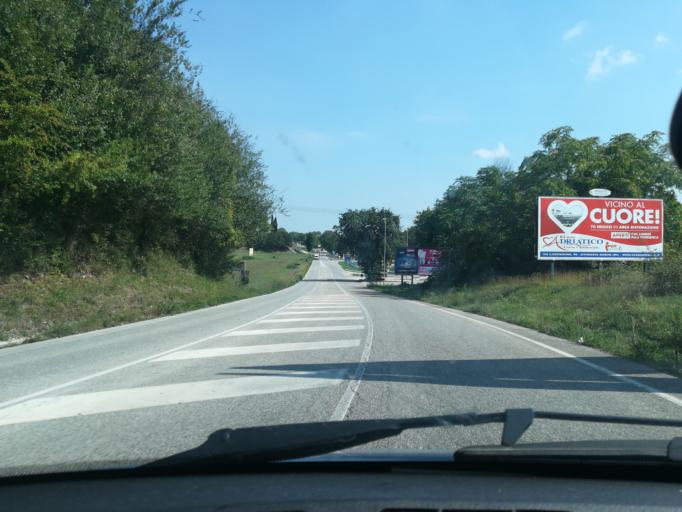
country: IT
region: The Marches
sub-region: Provincia di Macerata
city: Pollenza
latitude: 43.2245
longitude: 13.3374
